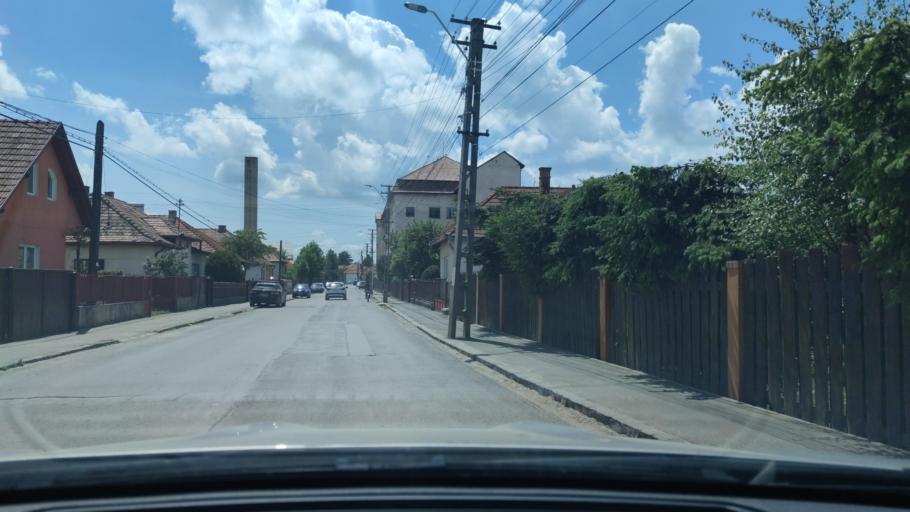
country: RO
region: Harghita
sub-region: Municipiul Gheorgheni
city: Gheorgheni
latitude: 46.7256
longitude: 25.5987
